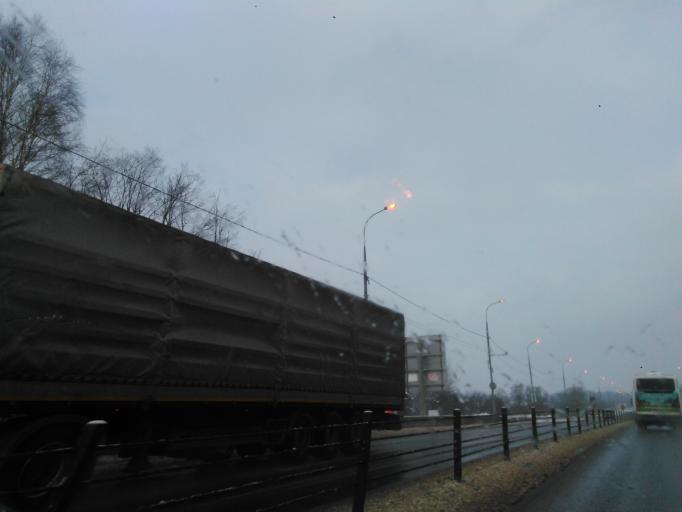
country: RU
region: Moskovskaya
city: Podosinki
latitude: 56.2135
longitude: 37.5217
